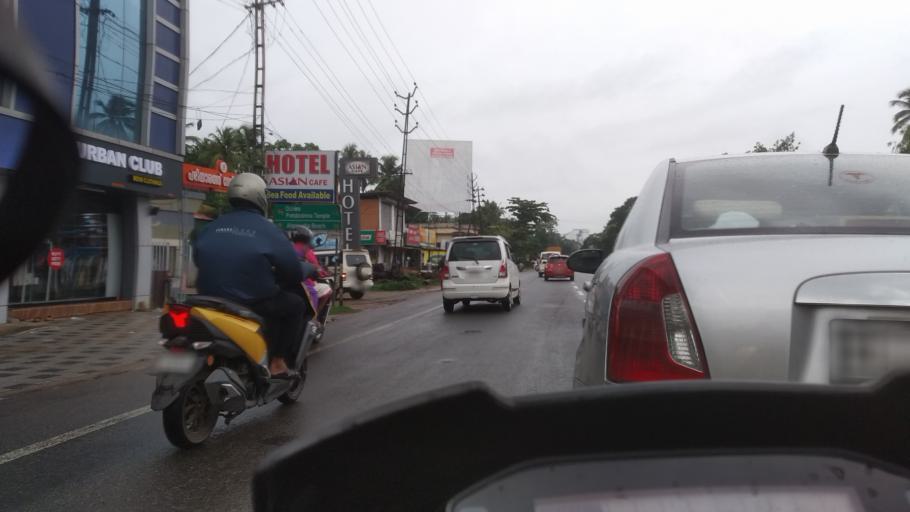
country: IN
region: Kerala
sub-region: Alappuzha
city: Kayankulam
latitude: 9.1269
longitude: 76.5165
